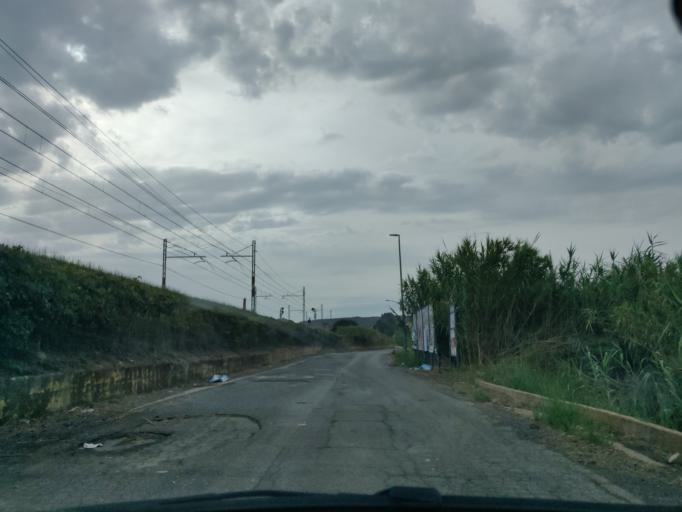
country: IT
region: Latium
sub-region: Citta metropolitana di Roma Capitale
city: Santa Marinella
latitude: 42.0407
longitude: 11.8945
